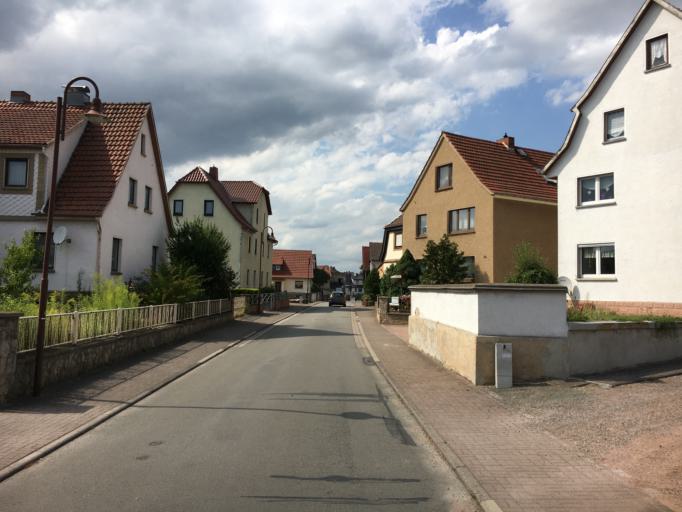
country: DE
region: Thuringia
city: Breitungen
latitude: 50.7630
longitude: 10.3290
